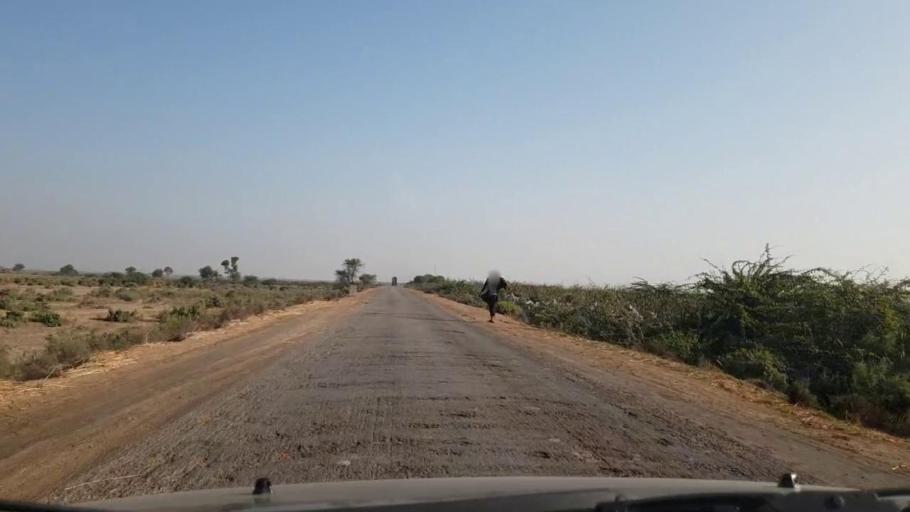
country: PK
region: Sindh
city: Tando Bago
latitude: 24.8300
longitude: 69.0160
